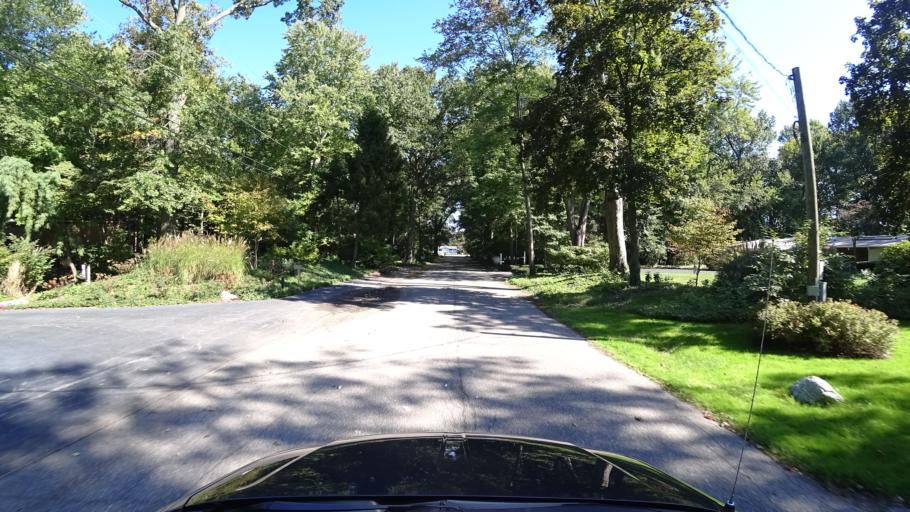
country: US
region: Indiana
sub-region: LaPorte County
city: Michigan City
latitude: 41.6935
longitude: -86.8879
